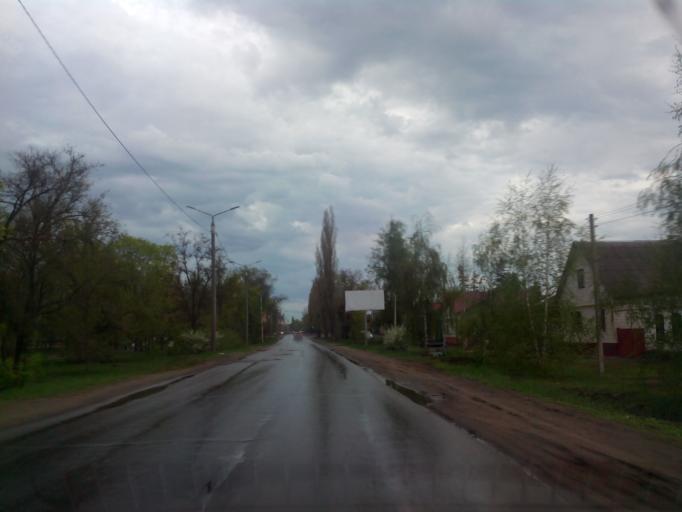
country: RU
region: Voronezj
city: Borisoglebsk
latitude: 51.3616
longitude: 42.0754
